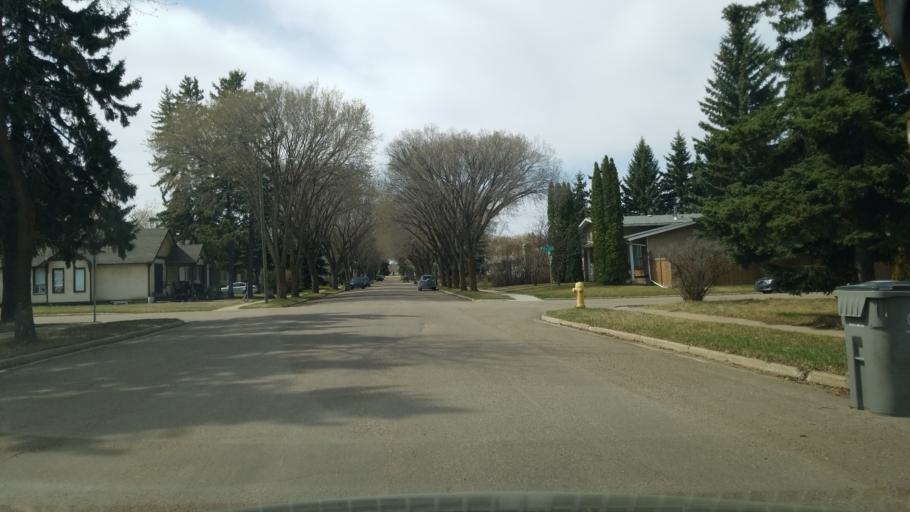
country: CA
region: Saskatchewan
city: Lloydminster
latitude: 53.2825
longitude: -110.0151
